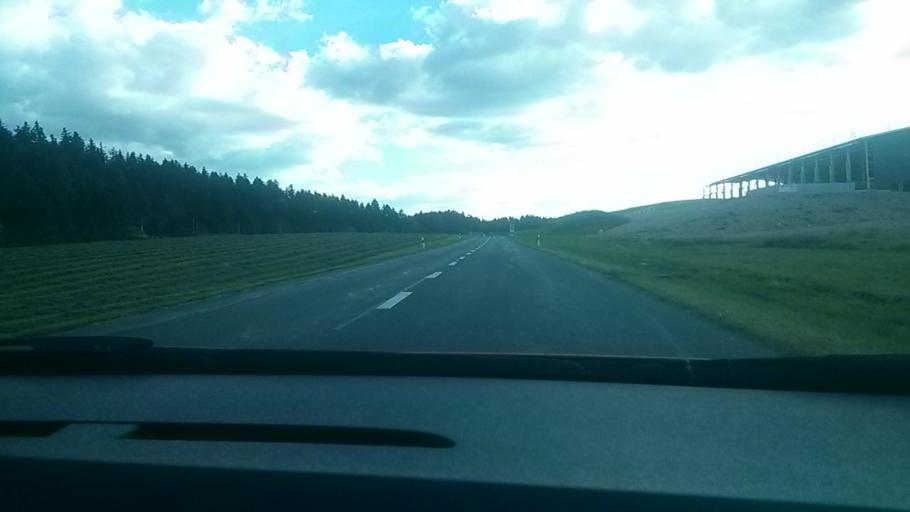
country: CH
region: Vaud
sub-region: Jura-Nord vaudois District
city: L'Abbaye
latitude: 46.6441
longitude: 6.2767
